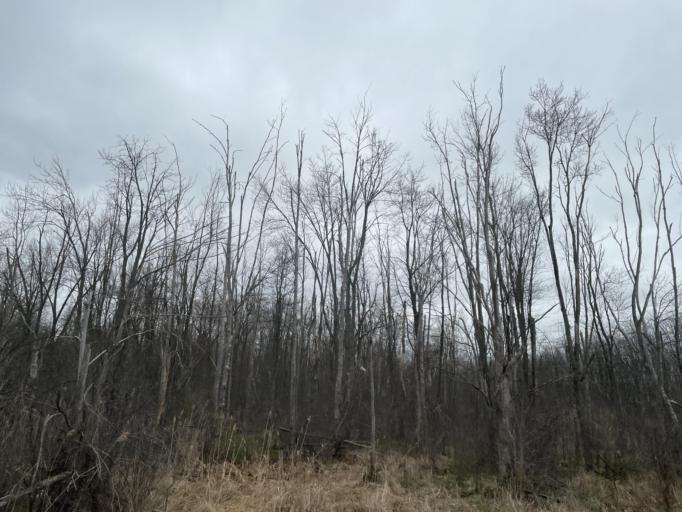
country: CA
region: Ontario
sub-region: Wellington County
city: Guelph
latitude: 43.5777
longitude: -80.2238
